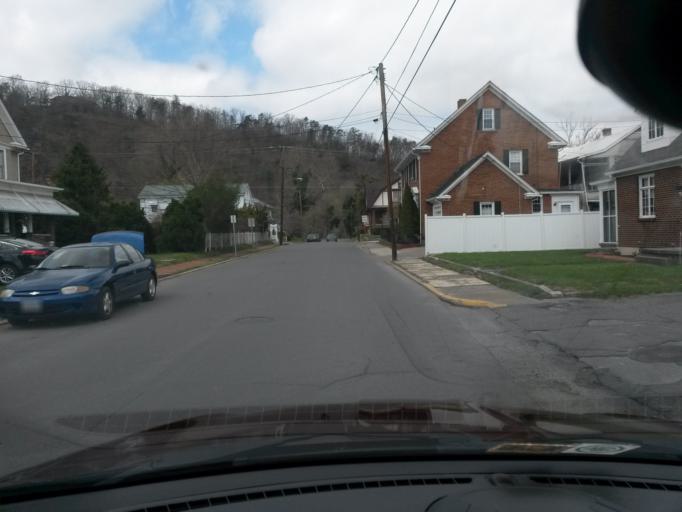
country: US
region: Virginia
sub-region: City of Covington
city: Covington
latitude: 37.7908
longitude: -79.9986
